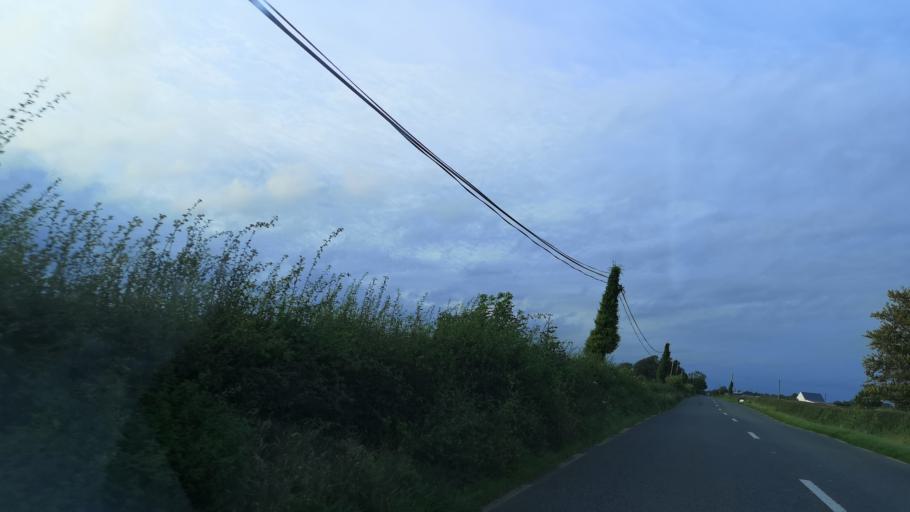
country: IE
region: Leinster
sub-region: Uibh Fhaili
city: Ferbane
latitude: 53.3210
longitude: -7.8215
